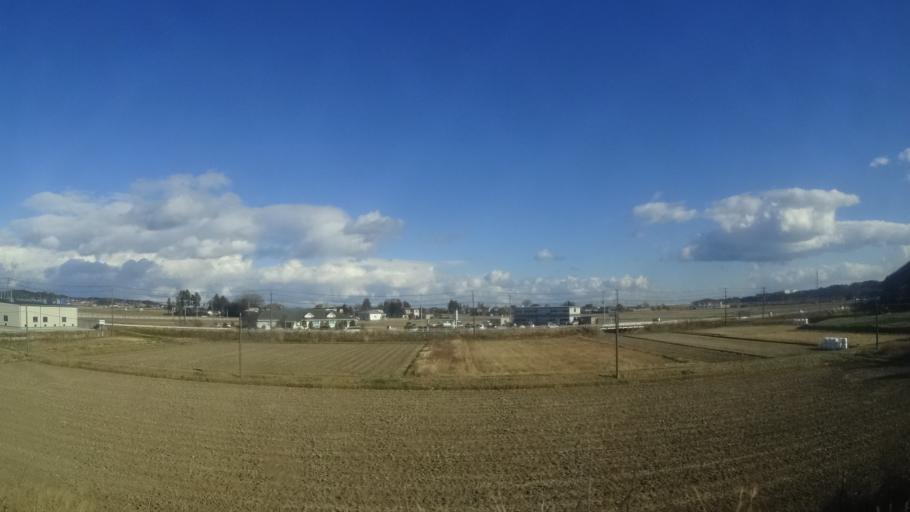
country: JP
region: Fukushima
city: Namie
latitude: 37.6917
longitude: 140.9735
